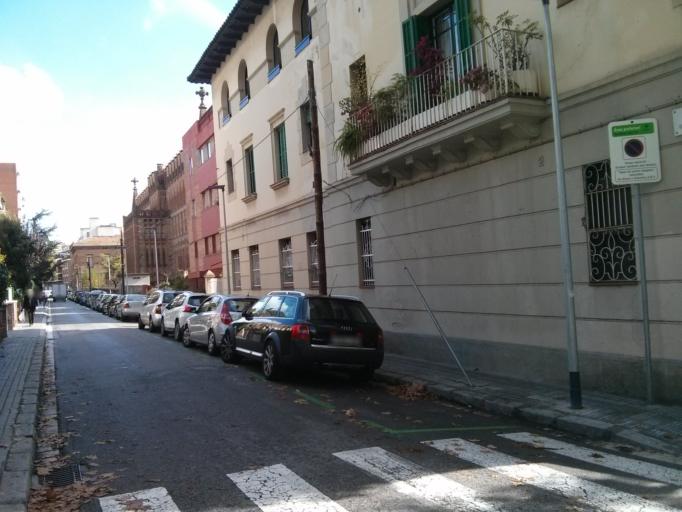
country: ES
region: Catalonia
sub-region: Provincia de Barcelona
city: Sarria-Sant Gervasi
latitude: 41.3997
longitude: 2.1317
